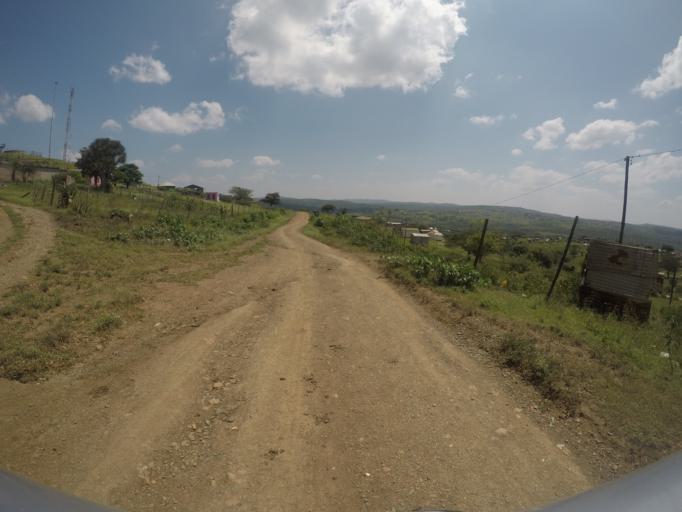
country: ZA
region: KwaZulu-Natal
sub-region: uThungulu District Municipality
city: Empangeni
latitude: -28.5978
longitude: 31.7413
